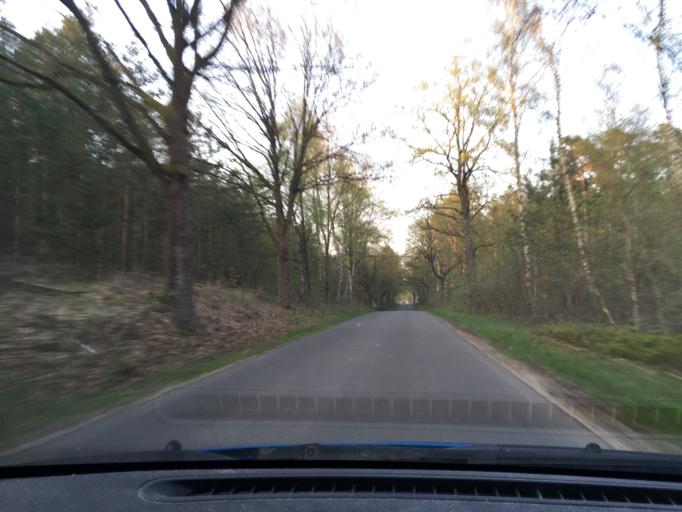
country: DE
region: Lower Saxony
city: Sudergellersen
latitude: 53.1936
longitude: 10.2777
